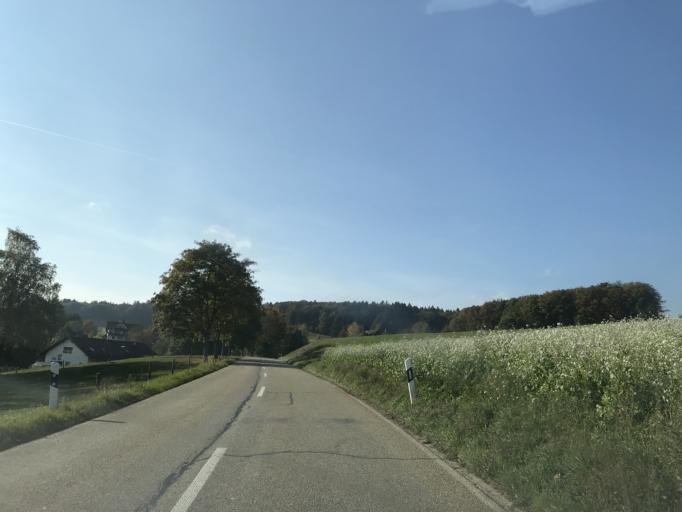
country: DE
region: Baden-Wuerttemberg
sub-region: Freiburg Region
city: Gorwihl
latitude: 47.6338
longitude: 8.0666
